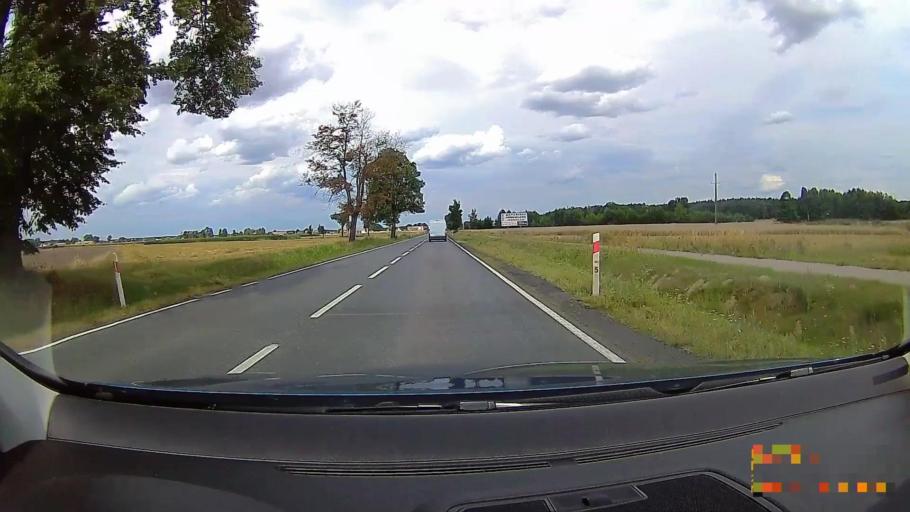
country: PL
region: Greater Poland Voivodeship
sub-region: Powiat koninski
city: Rychwal
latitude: 52.0866
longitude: 18.1633
